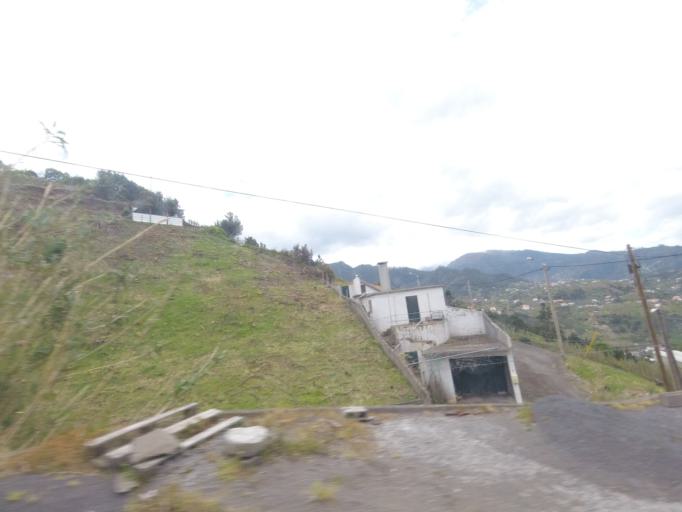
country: PT
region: Madeira
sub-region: Santana
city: Santana
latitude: 32.7642
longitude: -16.8143
